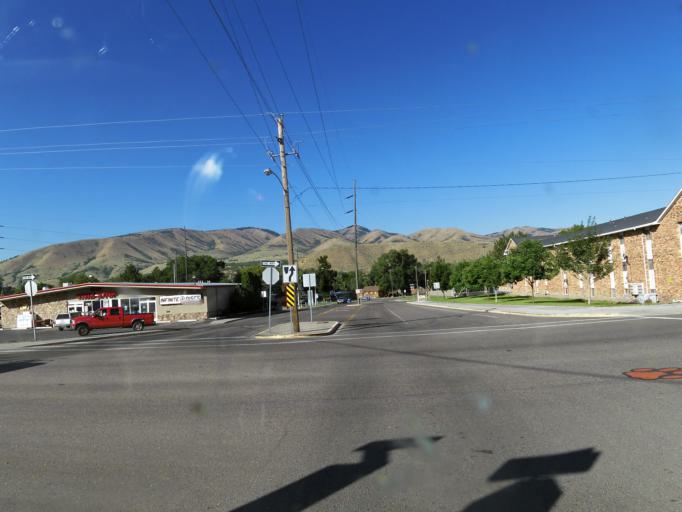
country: US
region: Idaho
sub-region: Bannock County
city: Pocatello
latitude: 42.8489
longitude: -112.4230
